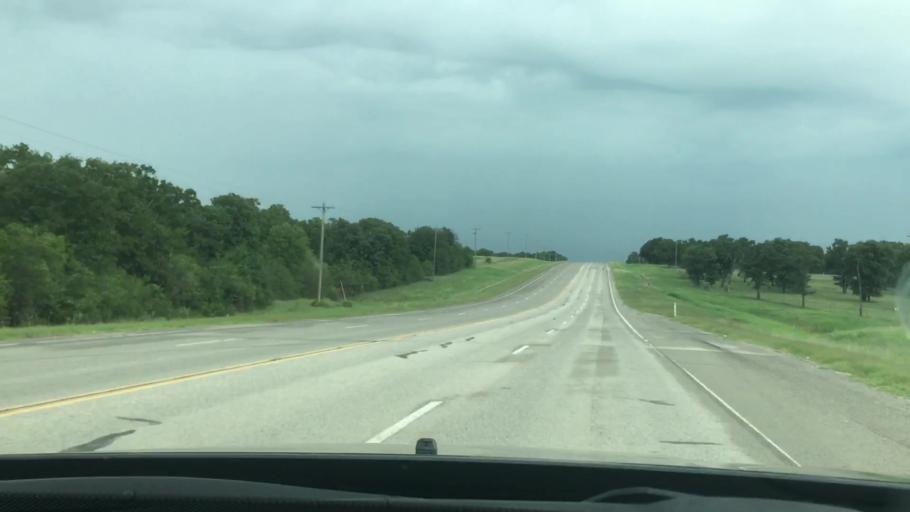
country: US
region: Oklahoma
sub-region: Carter County
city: Healdton
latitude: 34.1890
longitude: -97.4747
